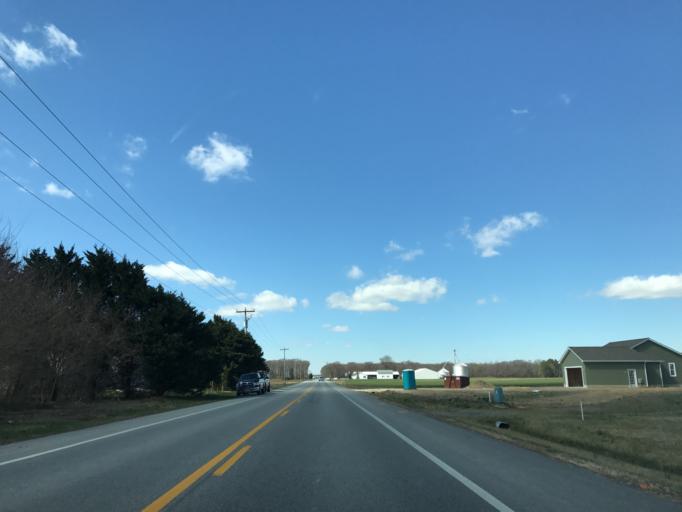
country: US
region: Maryland
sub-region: Caroline County
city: Greensboro
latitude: 39.0934
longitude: -75.8789
